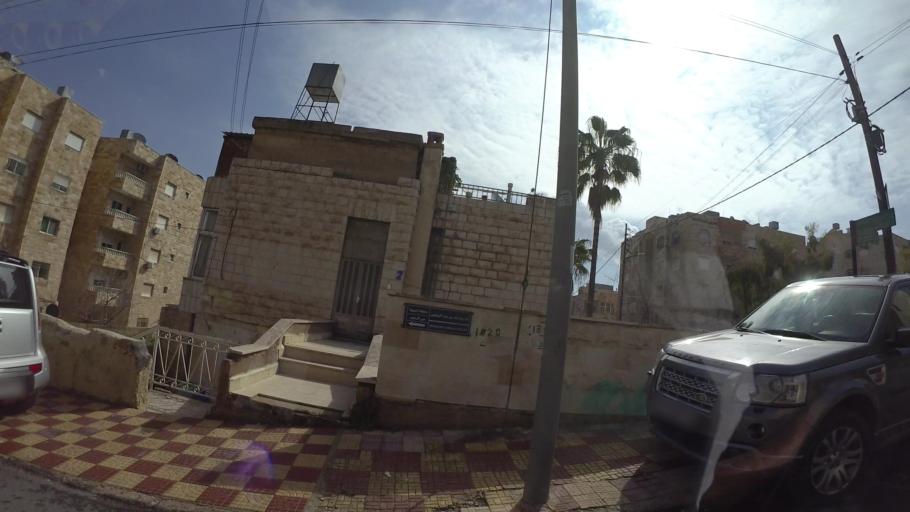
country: JO
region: Amman
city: Al Jubayhah
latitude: 31.9934
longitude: 35.9005
